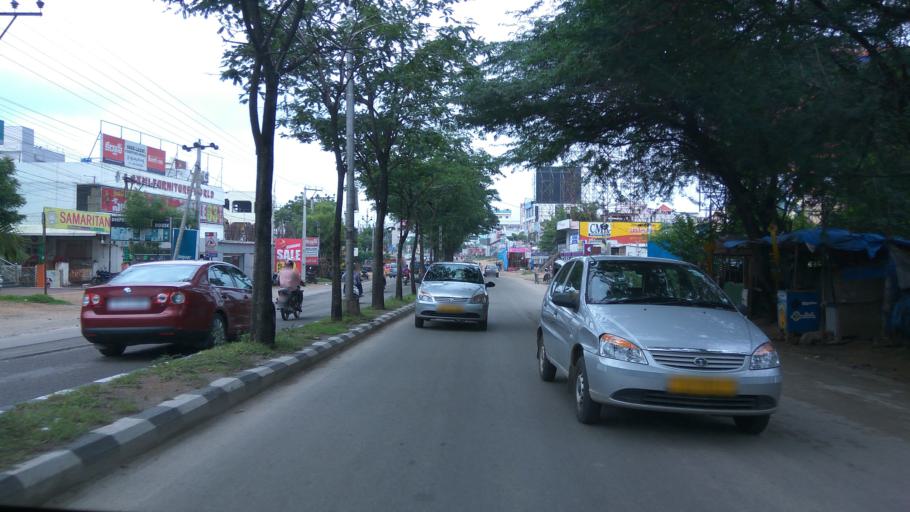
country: IN
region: Telangana
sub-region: Rangareddi
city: Secunderabad
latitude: 17.4833
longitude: 78.5417
